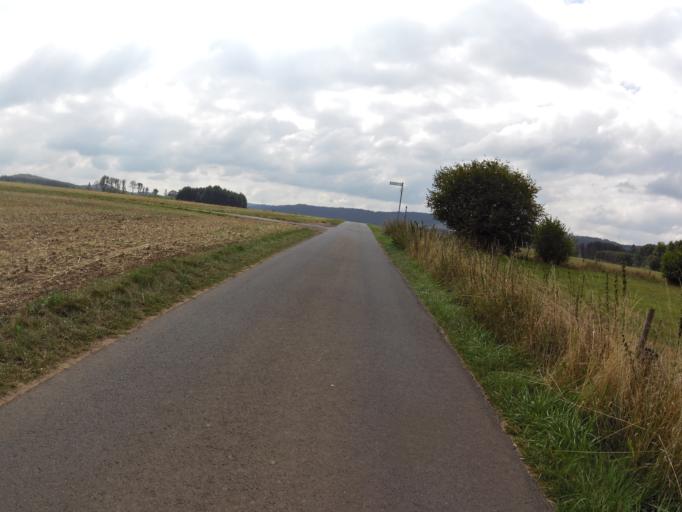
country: DE
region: Rheinland-Pfalz
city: Oberbettingen
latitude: 50.2873
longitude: 6.6471
